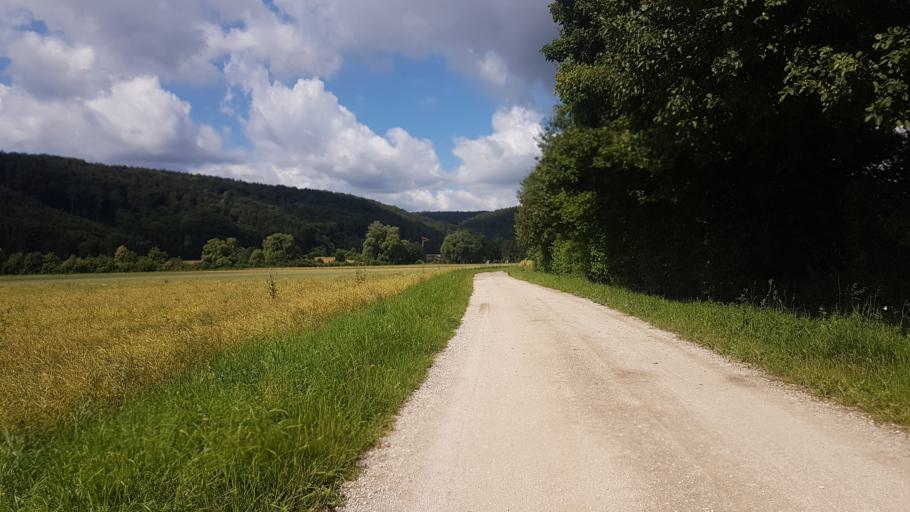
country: DE
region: Bavaria
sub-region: Upper Bavaria
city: Bohmfeld
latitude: 48.9236
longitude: 11.3608
